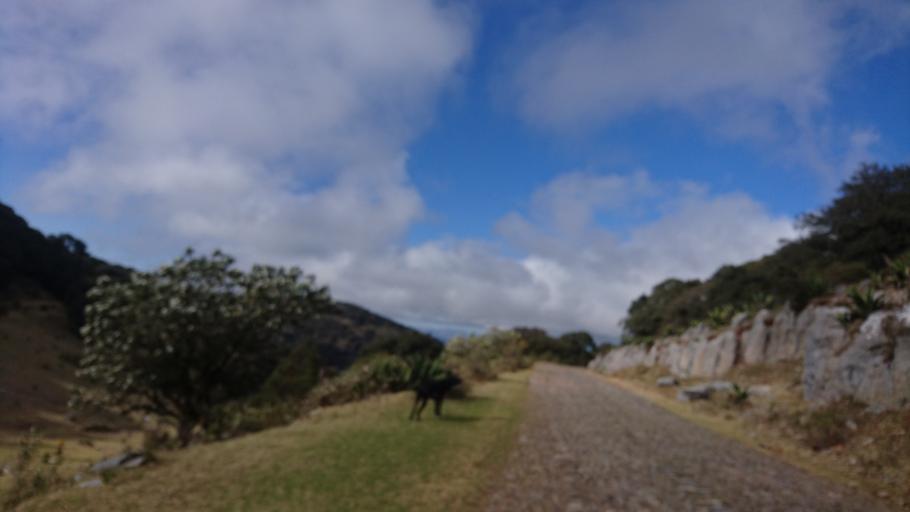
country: MX
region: San Luis Potosi
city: Zaragoza
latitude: 22.0714
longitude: -100.6417
